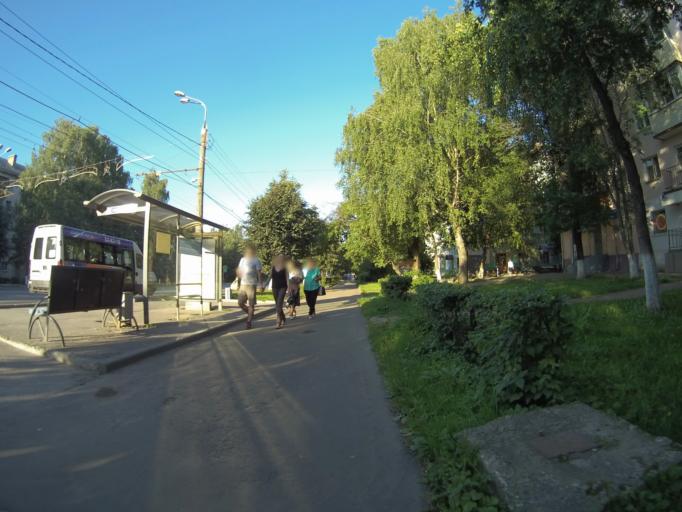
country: RU
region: Vladimir
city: Vladimir
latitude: 56.1209
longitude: 40.3764
